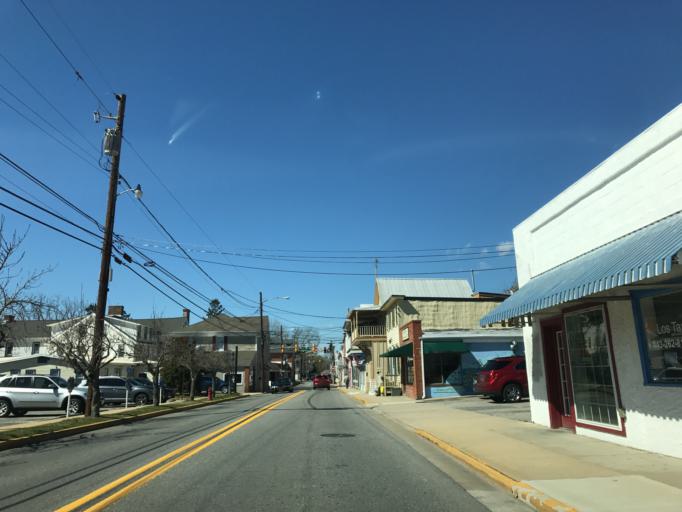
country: US
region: Maryland
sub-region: Queen Anne's County
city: Centreville
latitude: 39.0438
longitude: -76.0643
